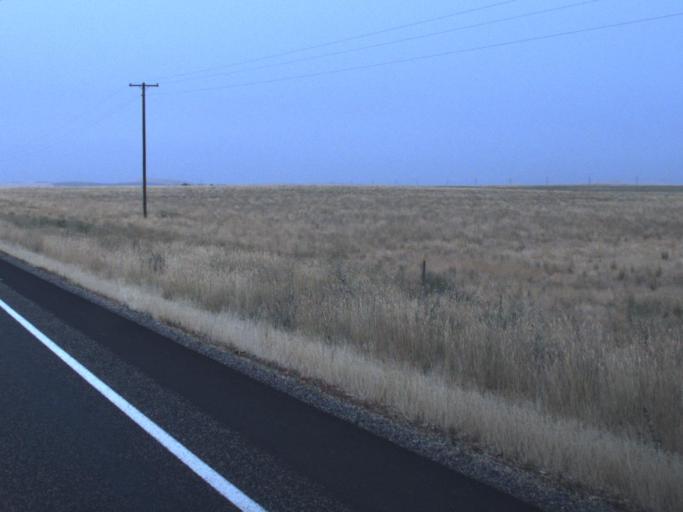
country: US
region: Washington
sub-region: Benton County
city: Benton City
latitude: 46.1480
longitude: -119.6010
